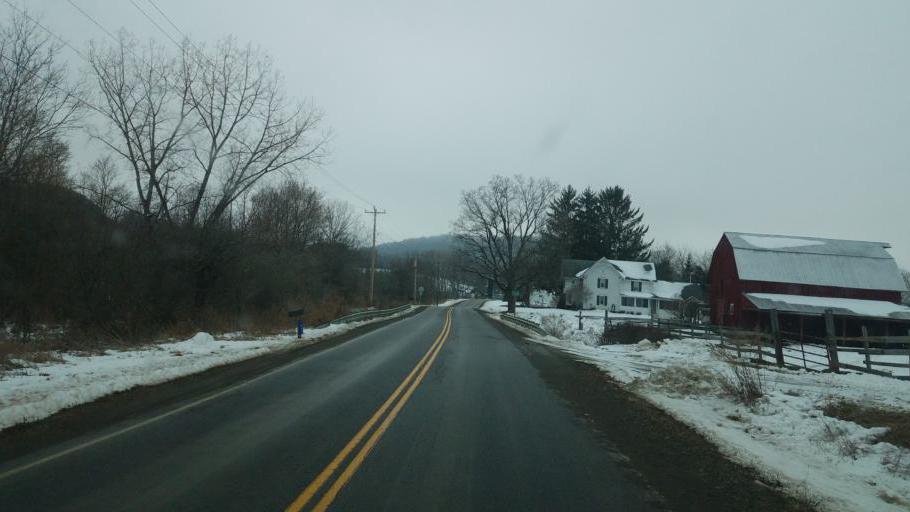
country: US
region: Pennsylvania
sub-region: Tioga County
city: Westfield
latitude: 42.0212
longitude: -77.5641
